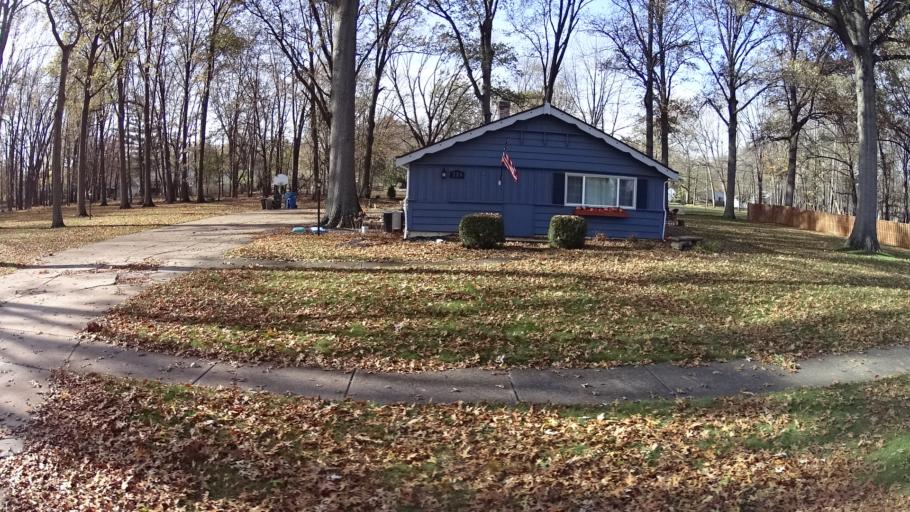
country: US
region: Ohio
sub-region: Lorain County
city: Avon Lake
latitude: 41.5060
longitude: -81.9951
